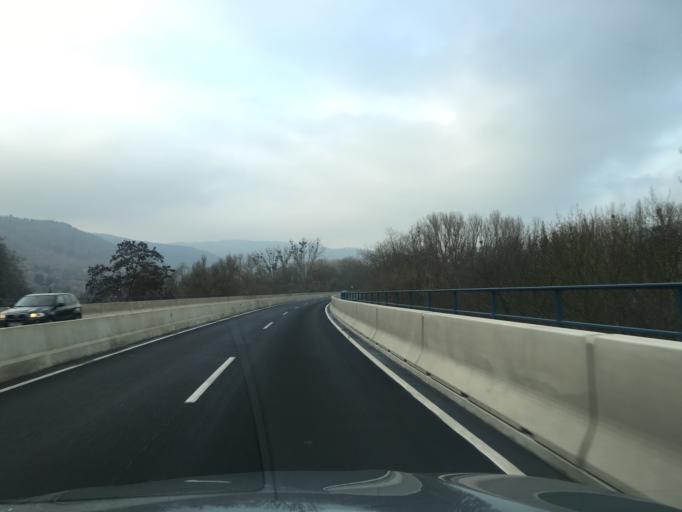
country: DE
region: Rheinland-Pfalz
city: Leutesdorf
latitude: 50.4468
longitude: 7.3800
